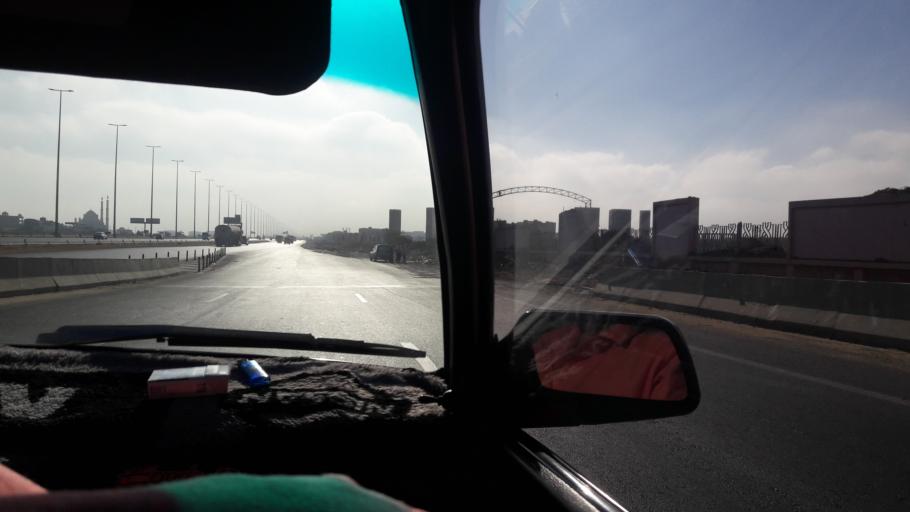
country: EG
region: Muhafazat al Qalyubiyah
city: Al Khankah
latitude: 30.1785
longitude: 31.5929
